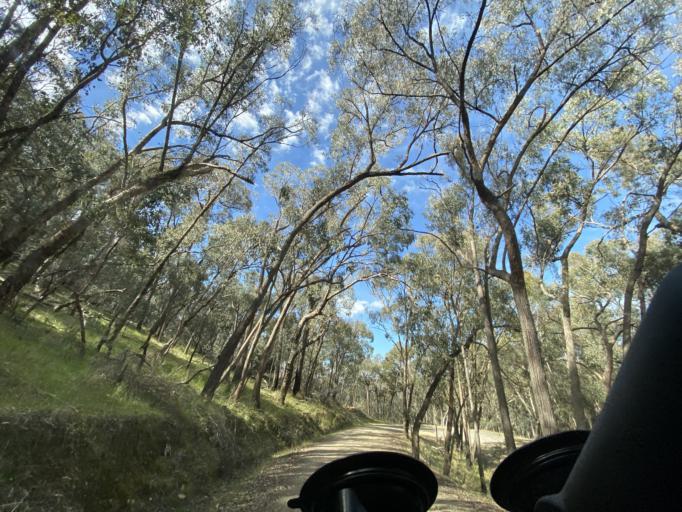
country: AU
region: Victoria
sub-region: Mansfield
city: Mansfield
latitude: -36.7974
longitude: 146.1143
